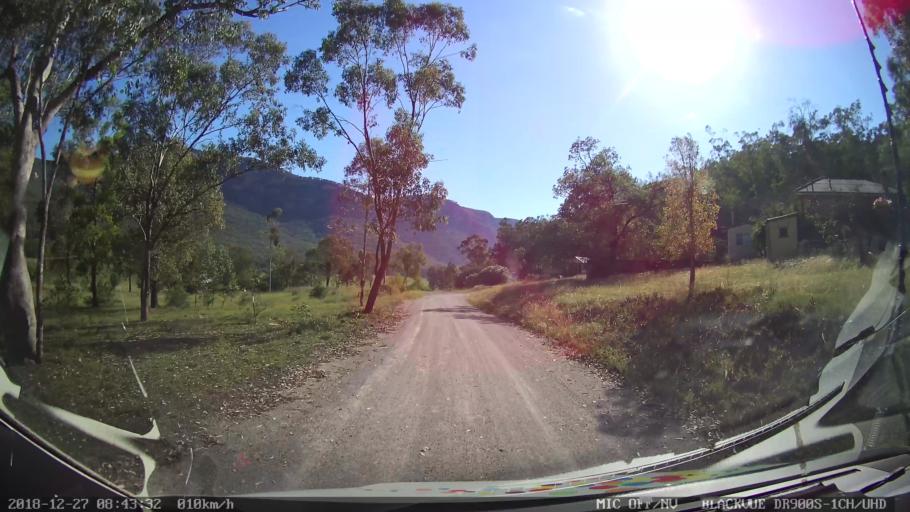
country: AU
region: New South Wales
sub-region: Lithgow
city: Portland
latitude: -33.1248
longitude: 150.2823
